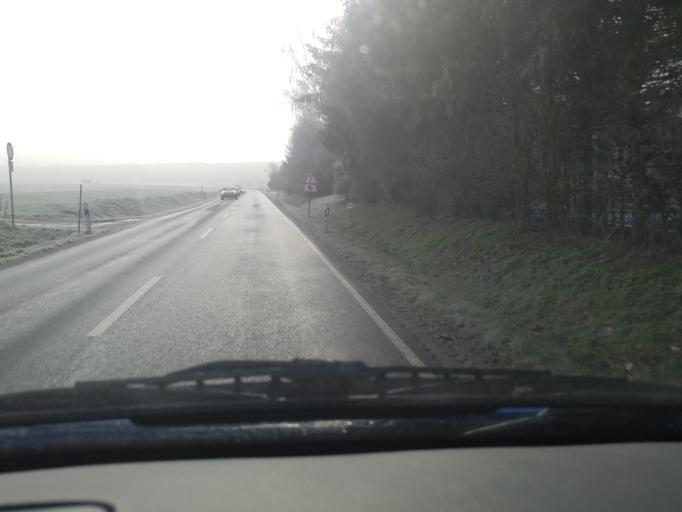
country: DE
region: Hesse
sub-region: Regierungsbezirk Darmstadt
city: Rosbach vor der Hohe
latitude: 50.2657
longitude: 8.7185
